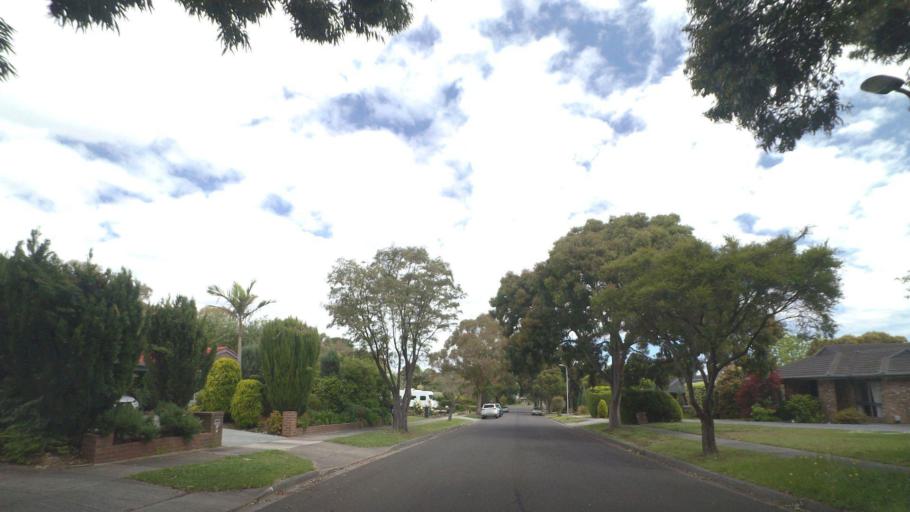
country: AU
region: Victoria
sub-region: Knox
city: Knoxfield
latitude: -37.8746
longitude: 145.2394
